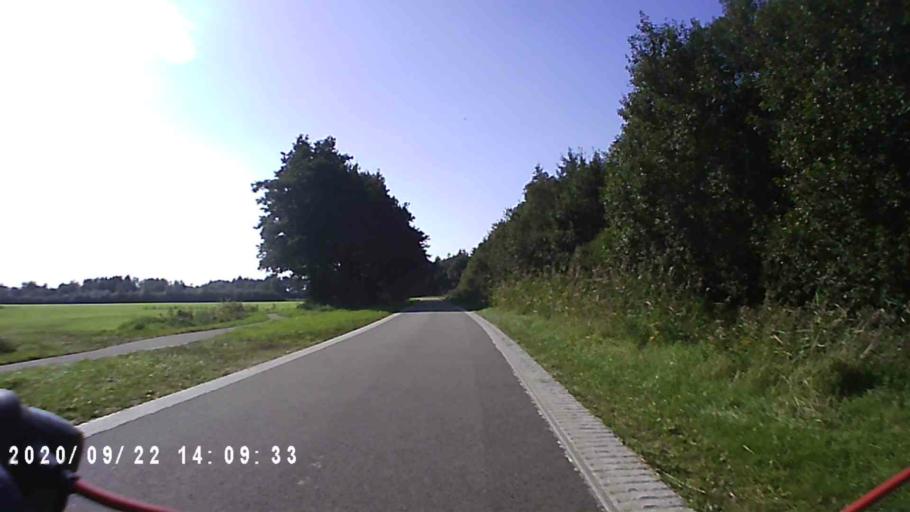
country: NL
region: Groningen
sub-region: Gemeente Leek
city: Leek
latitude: 53.0867
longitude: 6.4260
